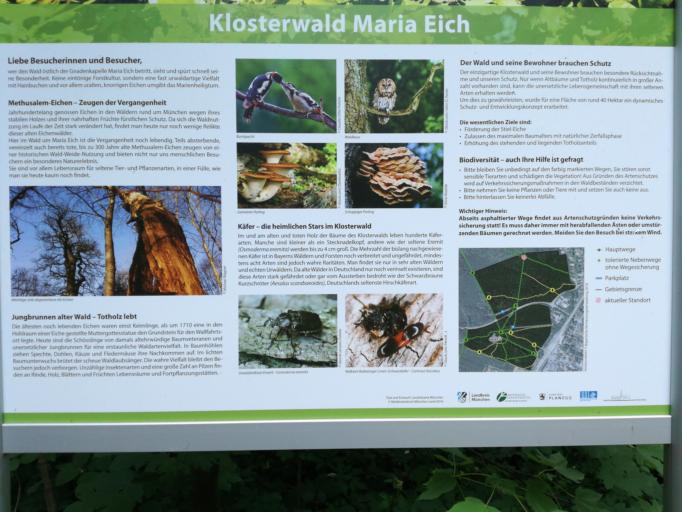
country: DE
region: Bavaria
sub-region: Upper Bavaria
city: Planegg
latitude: 48.1118
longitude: 11.4112
